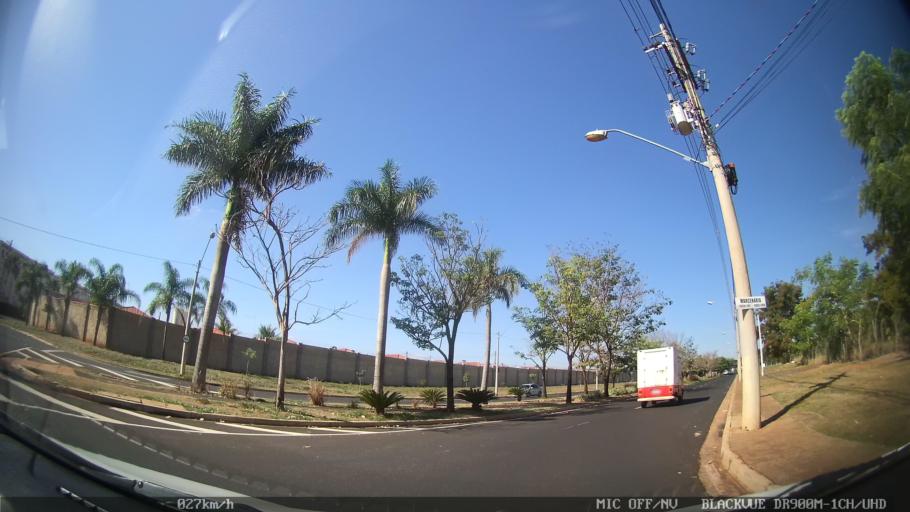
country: BR
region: Sao Paulo
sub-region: Ribeirao Preto
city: Ribeirao Preto
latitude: -21.2132
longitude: -47.7654
